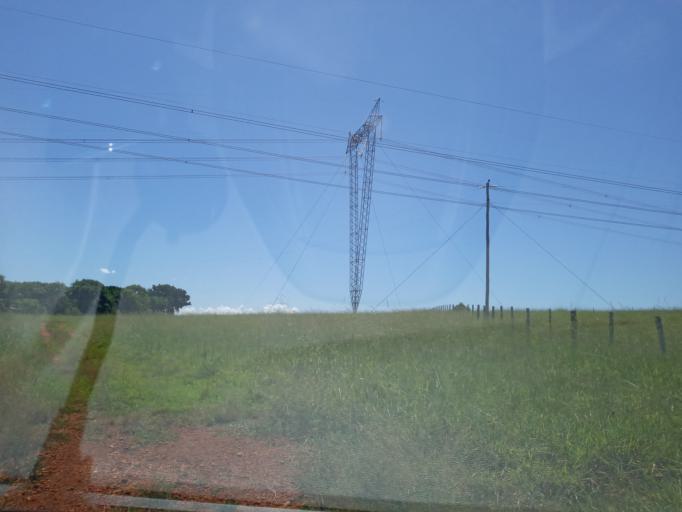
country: BR
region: Goias
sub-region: Itumbiara
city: Itumbiara
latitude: -18.3956
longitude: -49.1259
